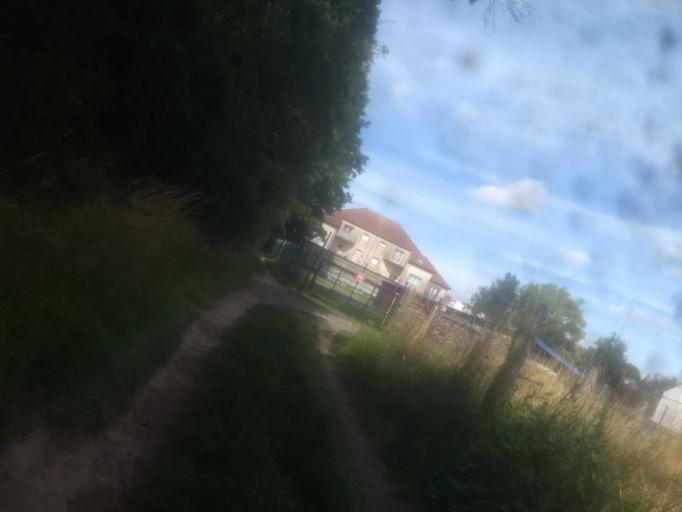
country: FR
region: Nord-Pas-de-Calais
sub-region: Departement du Pas-de-Calais
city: Agny
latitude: 50.2613
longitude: 2.7558
